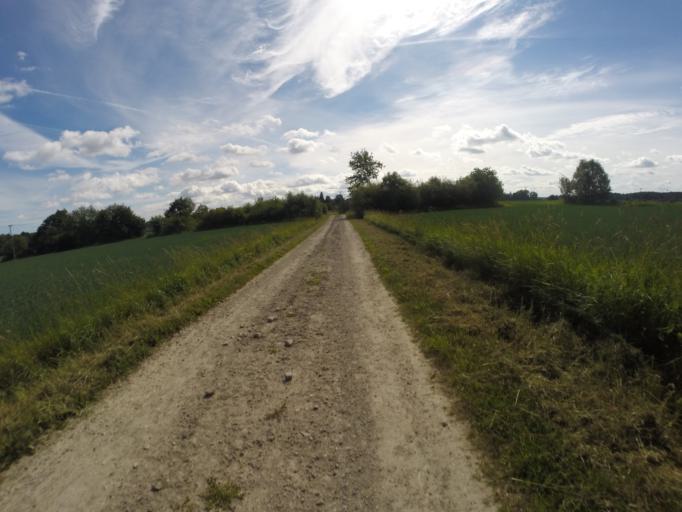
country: SE
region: Soedermanland
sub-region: Eskilstuna Kommun
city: Kvicksund
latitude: 59.4429
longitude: 16.3026
